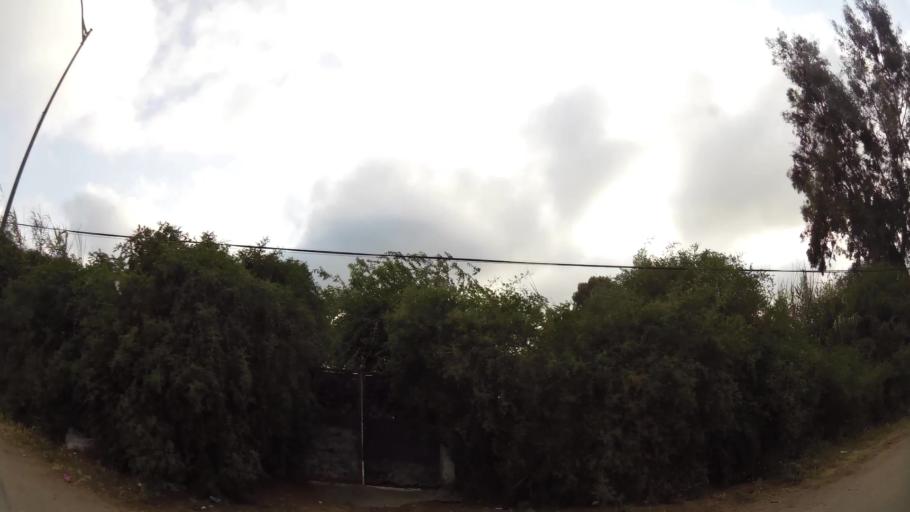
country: MA
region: Rabat-Sale-Zemmour-Zaer
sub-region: Skhirate-Temara
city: Temara
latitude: 33.9477
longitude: -6.8481
